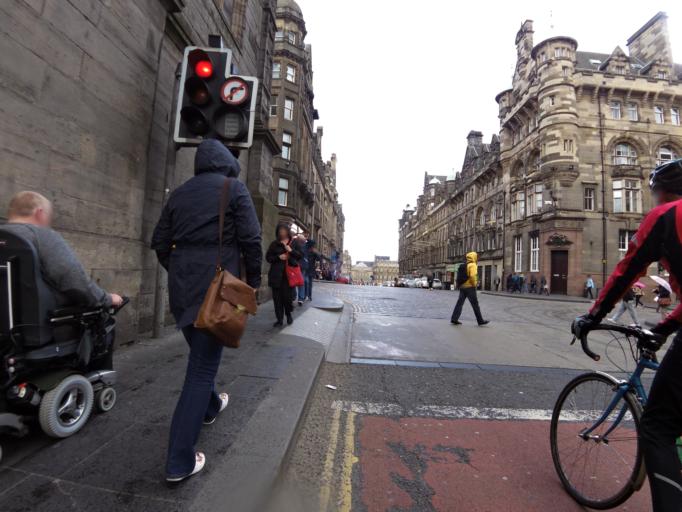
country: GB
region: Scotland
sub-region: Edinburgh
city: Edinburgh
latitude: 55.9499
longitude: -3.1875
